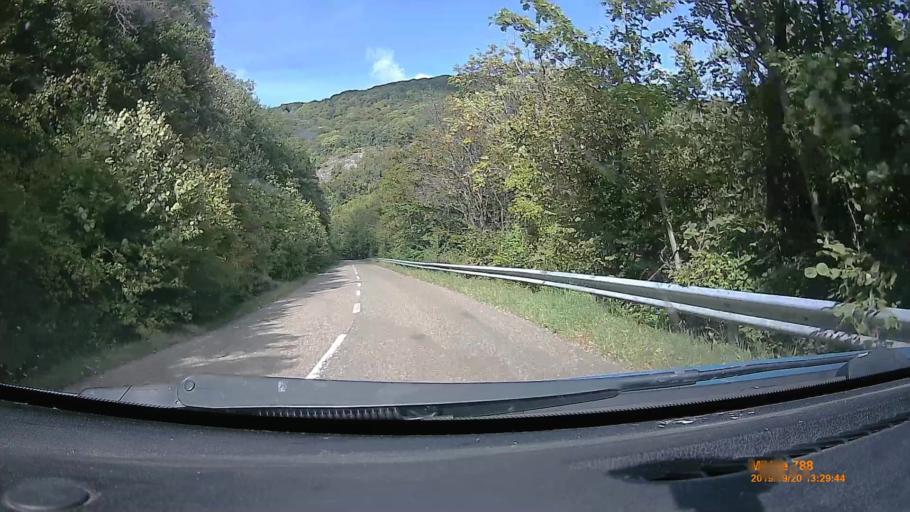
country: HU
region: Heves
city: Szilvasvarad
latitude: 48.0543
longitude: 20.4844
